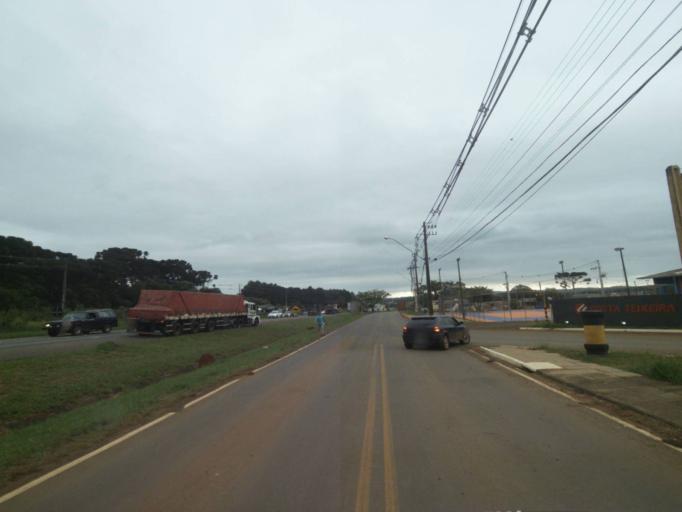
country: BR
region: Parana
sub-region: Telemaco Borba
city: Telemaco Borba
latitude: -24.3774
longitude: -50.6674
